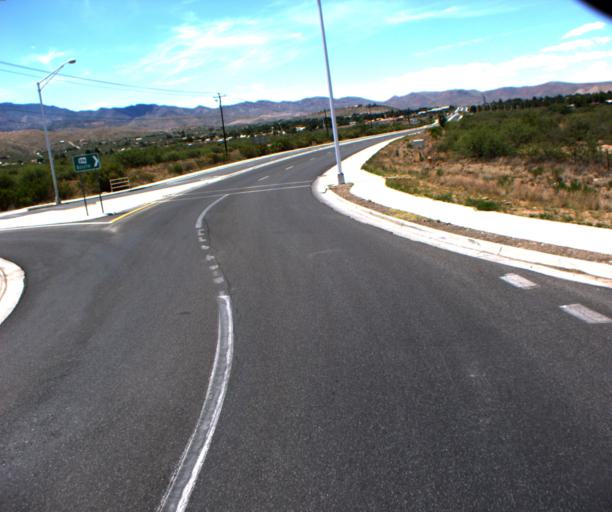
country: US
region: Arizona
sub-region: Yavapai County
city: Clarkdale
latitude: 34.7472
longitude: -112.0449
